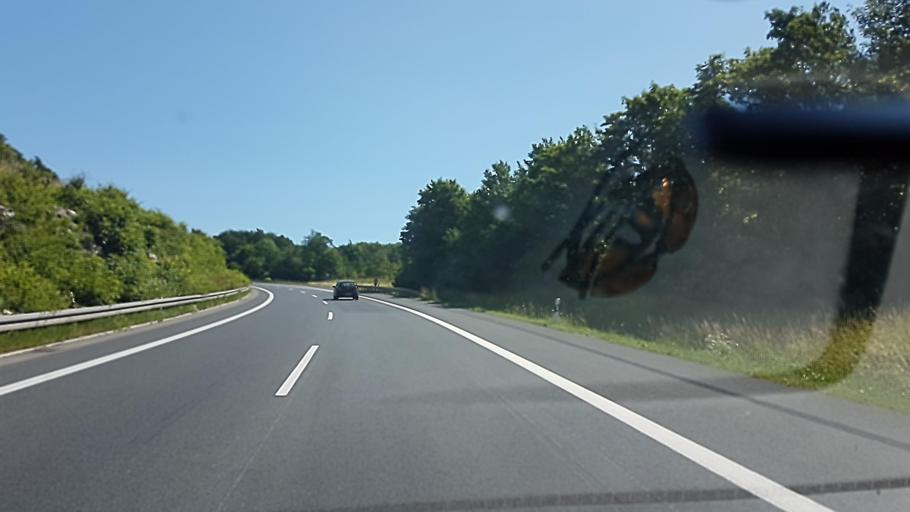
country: DE
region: Bavaria
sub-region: Upper Franconia
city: Poxdorf
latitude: 49.9827
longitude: 11.0939
